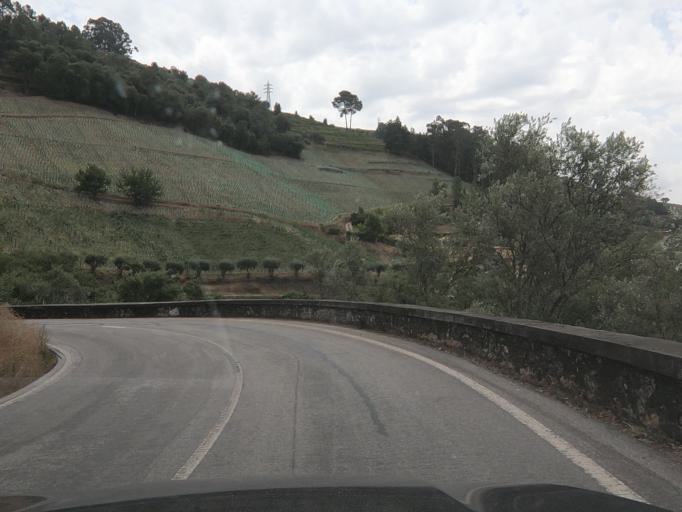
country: PT
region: Vila Real
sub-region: Santa Marta de Penaguiao
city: Santa Marta de Penaguiao
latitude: 41.2355
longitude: -7.7637
